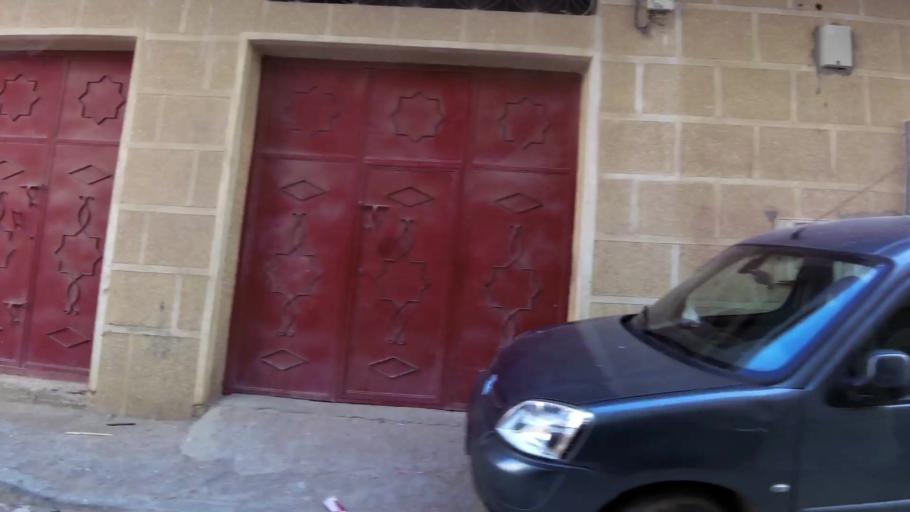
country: MA
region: Tanger-Tetouan
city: Tetouan
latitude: 35.5898
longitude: -5.3507
